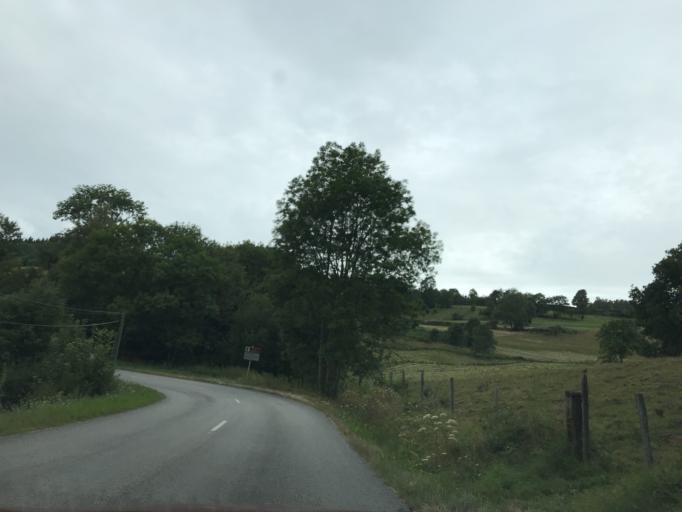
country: FR
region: Rhone-Alpes
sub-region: Departement de la Loire
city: Sail-sous-Couzan
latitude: 45.7013
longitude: 3.8672
